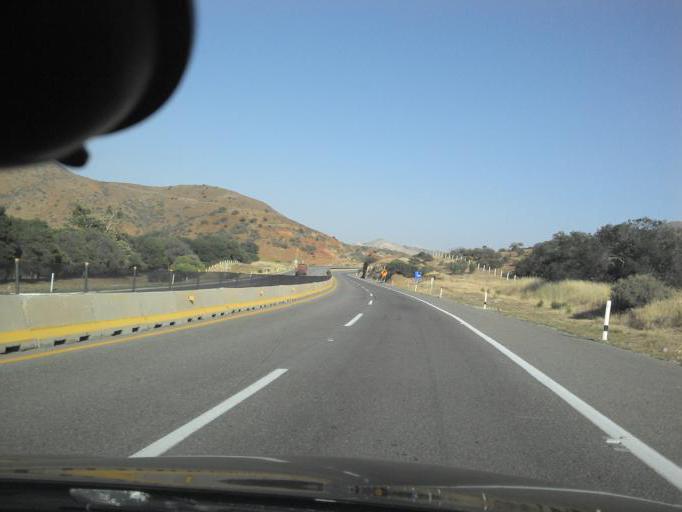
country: MX
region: Baja California
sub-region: Tijuana
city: El Nino
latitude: 32.5499
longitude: -116.8026
